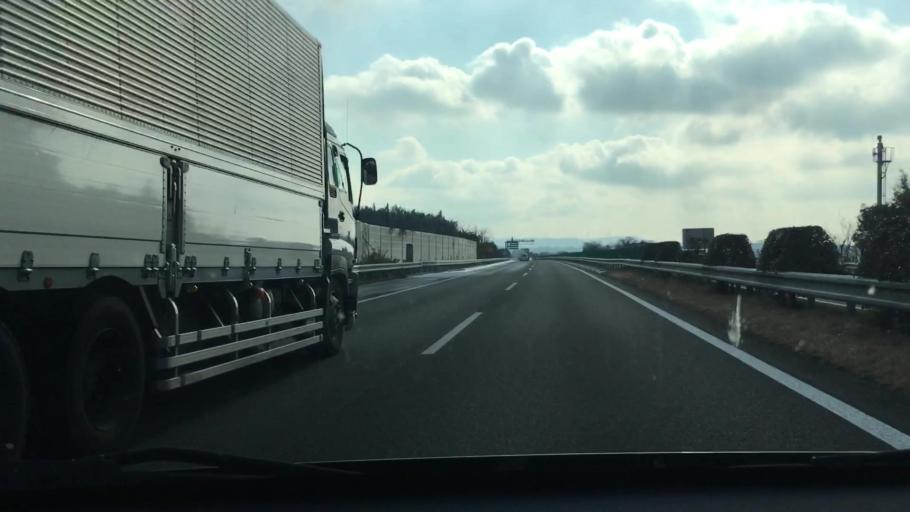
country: JP
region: Kumamoto
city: Uto
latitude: 32.7237
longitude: 130.7715
